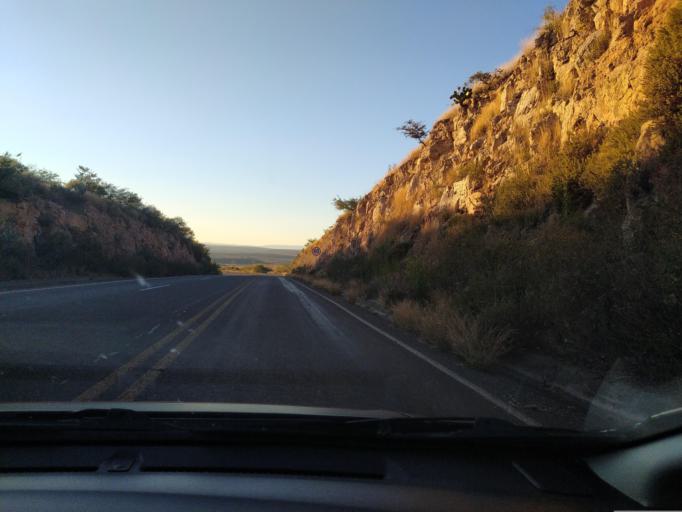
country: MX
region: Jalisco
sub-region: San Julian
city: Colonia Veintitres de Mayo
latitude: 21.0090
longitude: -102.2697
